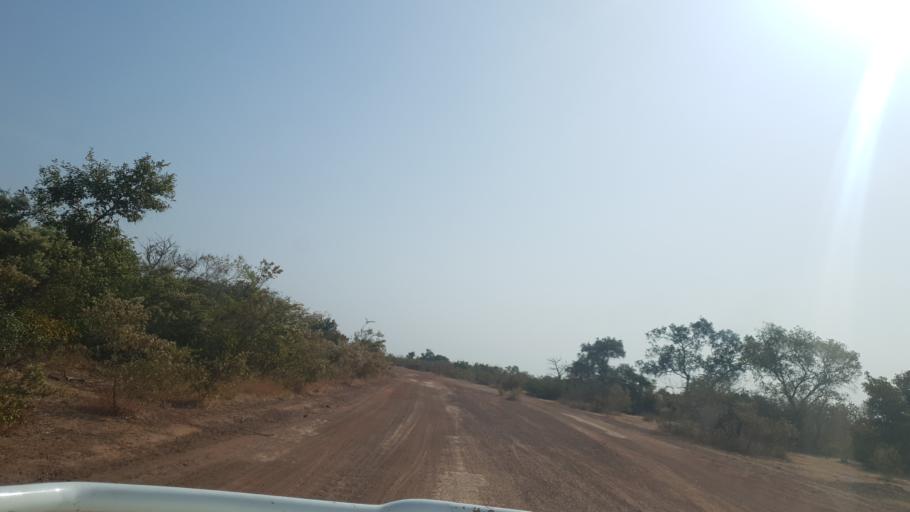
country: ML
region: Koulikoro
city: Dioila
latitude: 12.6676
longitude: -6.6993
